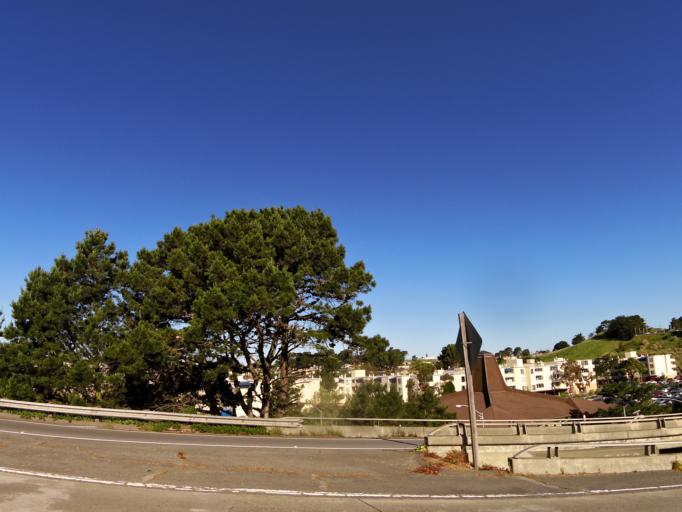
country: US
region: California
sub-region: San Mateo County
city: Colma
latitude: 37.6756
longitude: -122.4729
